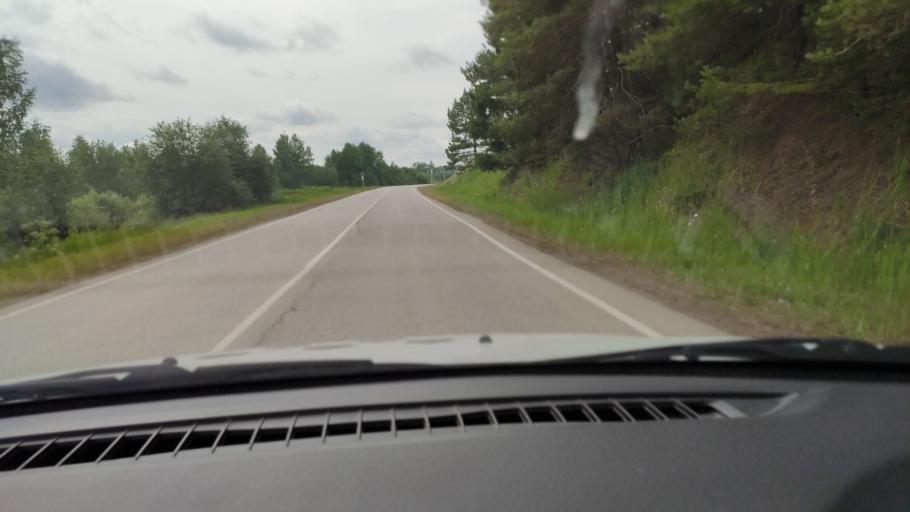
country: RU
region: Perm
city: Kukushtan
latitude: 57.4872
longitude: 56.6204
